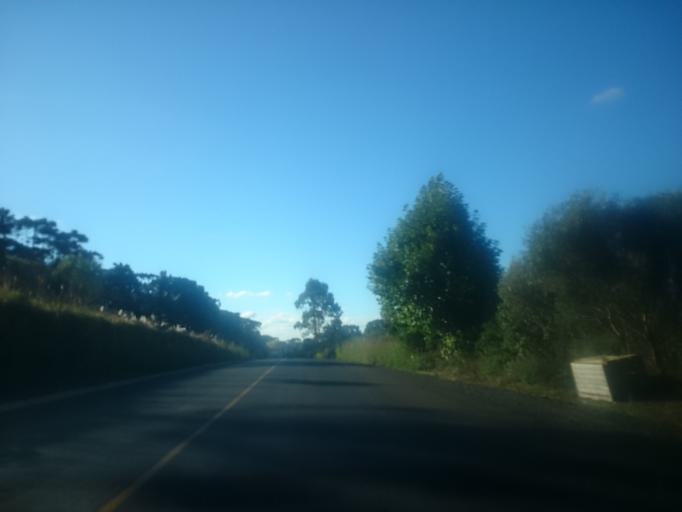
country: BR
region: Santa Catarina
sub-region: Sao Joaquim
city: Sao Joaquim
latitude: -28.2072
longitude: -49.9854
